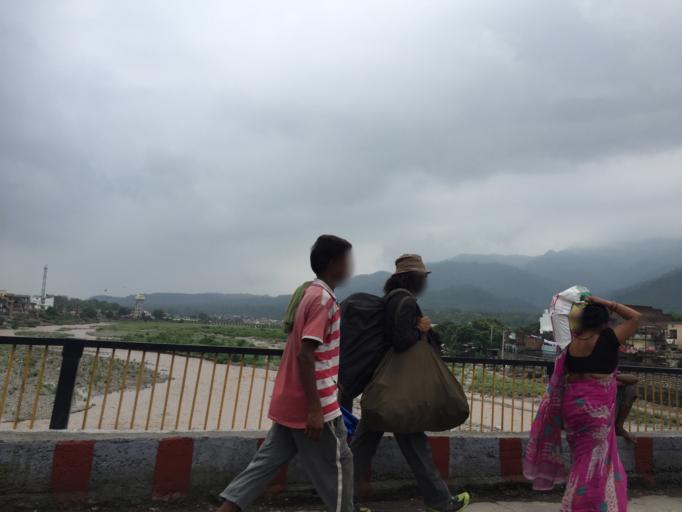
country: IN
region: Uttarakhand
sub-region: Dehradun
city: Rishikesh
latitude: 30.1087
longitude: 78.3015
